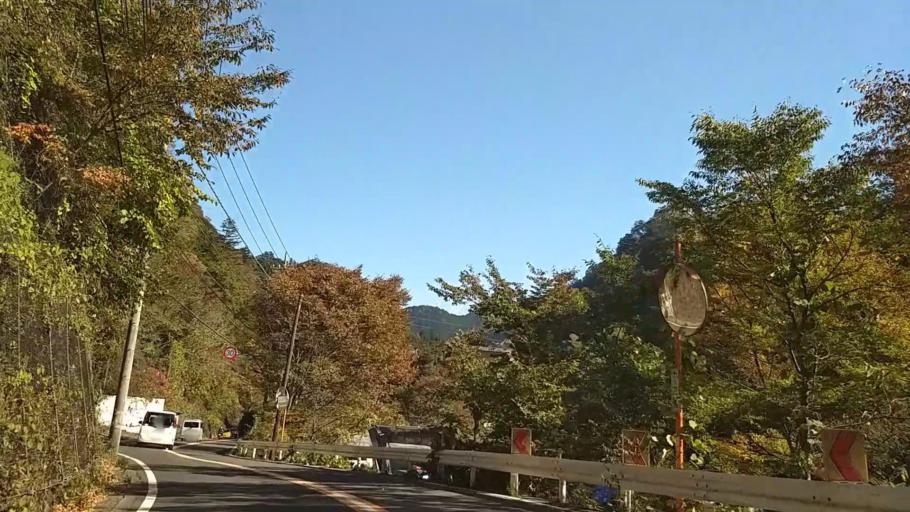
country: JP
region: Tokyo
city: Itsukaichi
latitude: 35.7938
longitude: 139.0484
